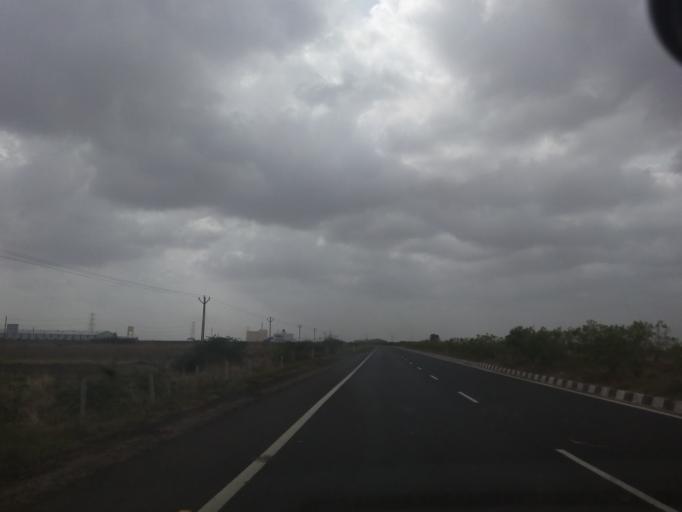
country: IN
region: Gujarat
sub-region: Rajkot
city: Morbi
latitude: 23.0522
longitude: 70.8676
